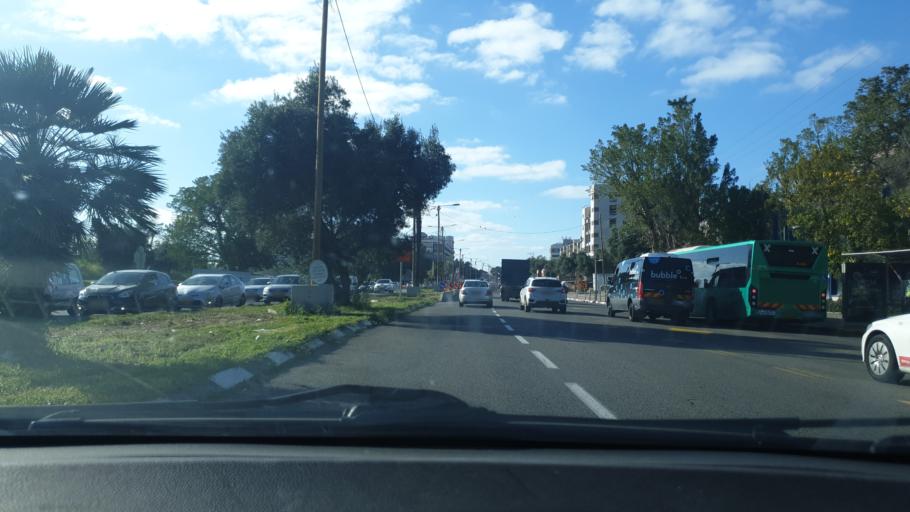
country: IL
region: Tel Aviv
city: Yafo
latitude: 32.0390
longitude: 34.7777
